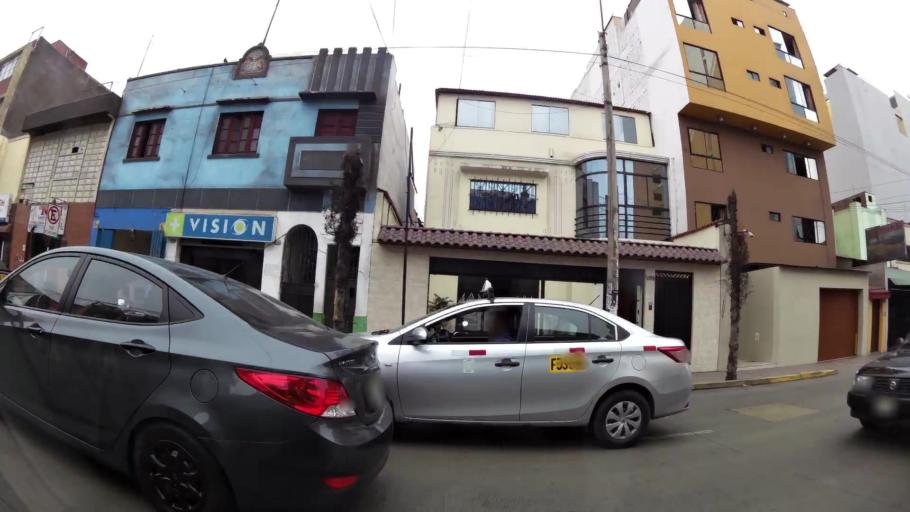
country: PE
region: Lima
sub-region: Lima
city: San Isidro
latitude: -12.0838
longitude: -77.0334
